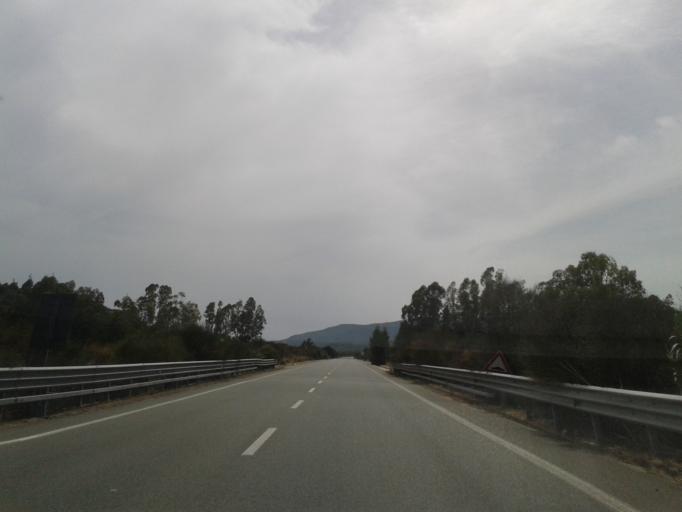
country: IT
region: Sardinia
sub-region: Provincia di Cagliari
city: Olia Speciosa
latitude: 39.2517
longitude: 9.5291
